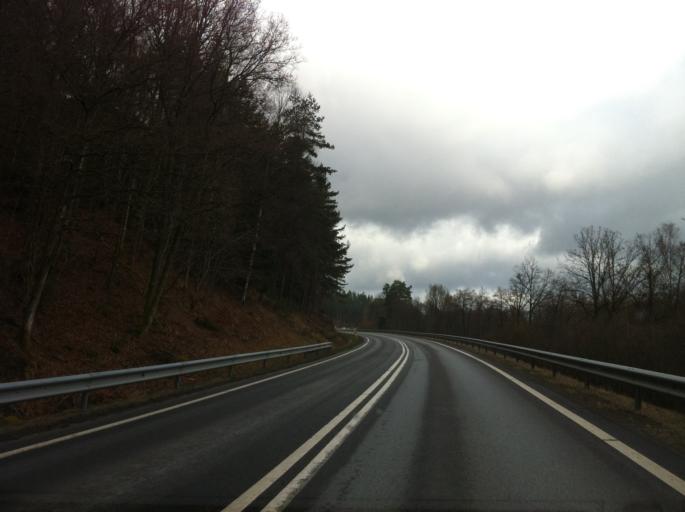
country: SE
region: Halland
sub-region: Halmstads Kommun
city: Oskarstrom
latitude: 56.8382
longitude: 12.9797
